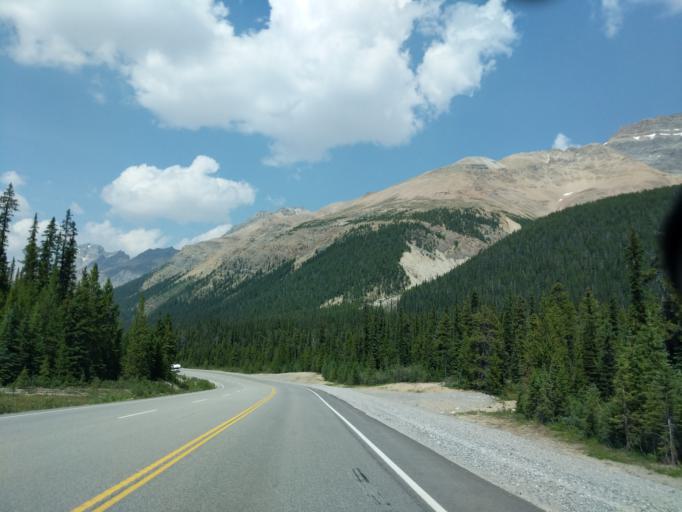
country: CA
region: Alberta
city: Lake Louise
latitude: 51.7276
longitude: -116.5010
